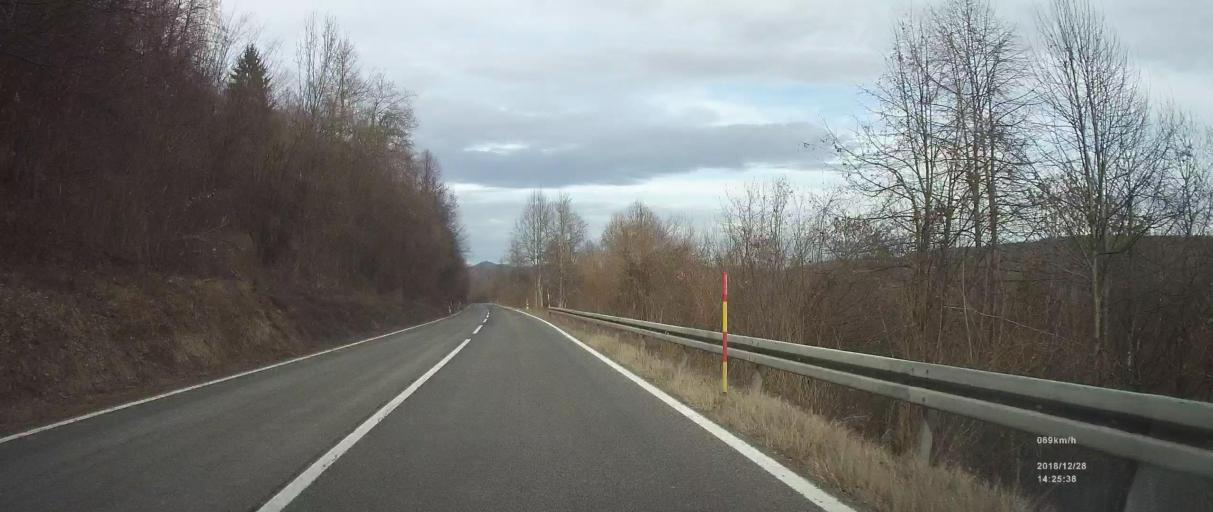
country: HR
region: Primorsko-Goranska
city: Vrbovsko
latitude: 45.3959
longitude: 15.1072
